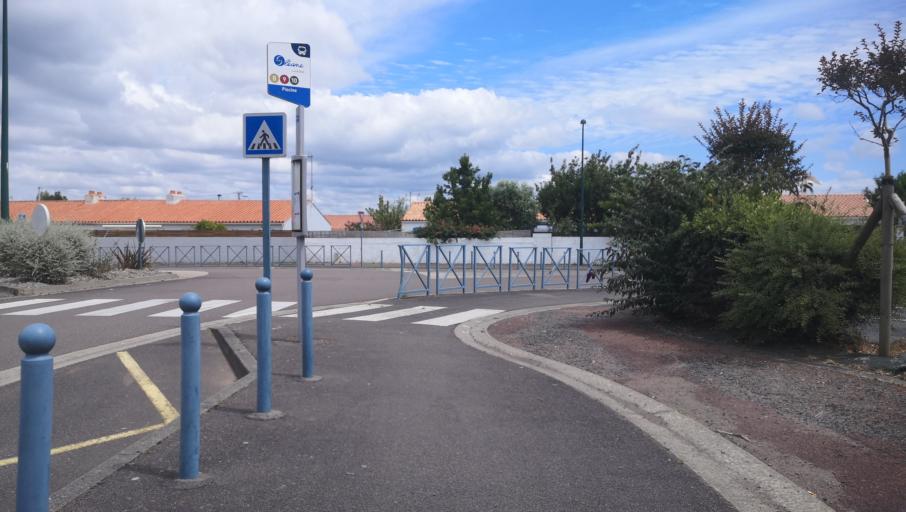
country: FR
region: Pays de la Loire
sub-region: Departement de la Vendee
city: Les Sables-d'Olonne
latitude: 46.5115
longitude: -1.7725
